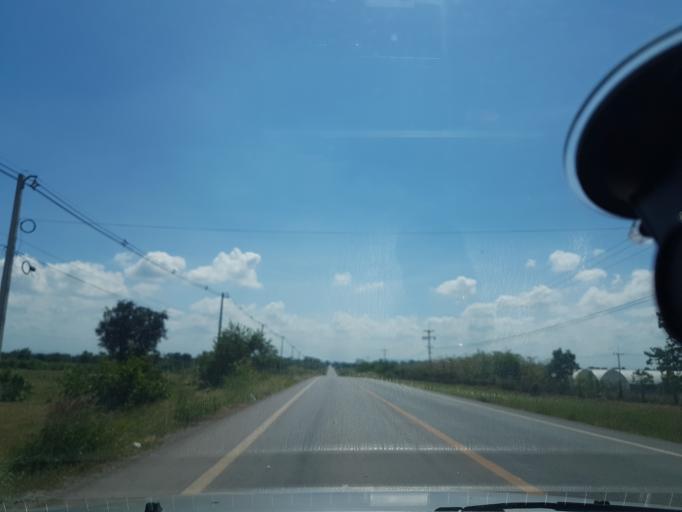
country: TH
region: Lop Buri
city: Phatthana Nikhom
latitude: 14.9629
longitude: 101.0072
